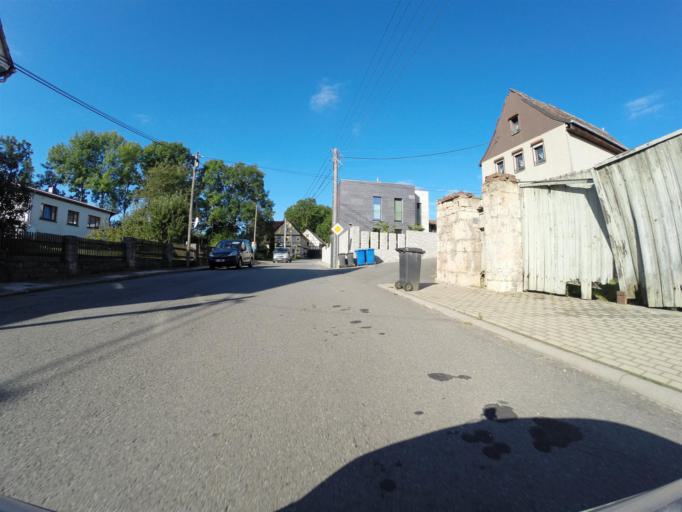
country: DE
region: Thuringia
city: Lehnstedt
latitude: 50.9128
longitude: 11.4204
